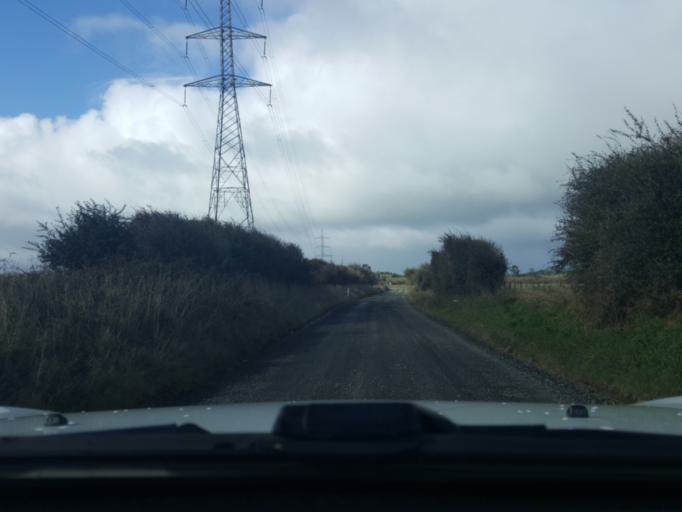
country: NZ
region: Waikato
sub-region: Waikato District
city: Te Kauwhata
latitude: -37.4154
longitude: 175.0653
